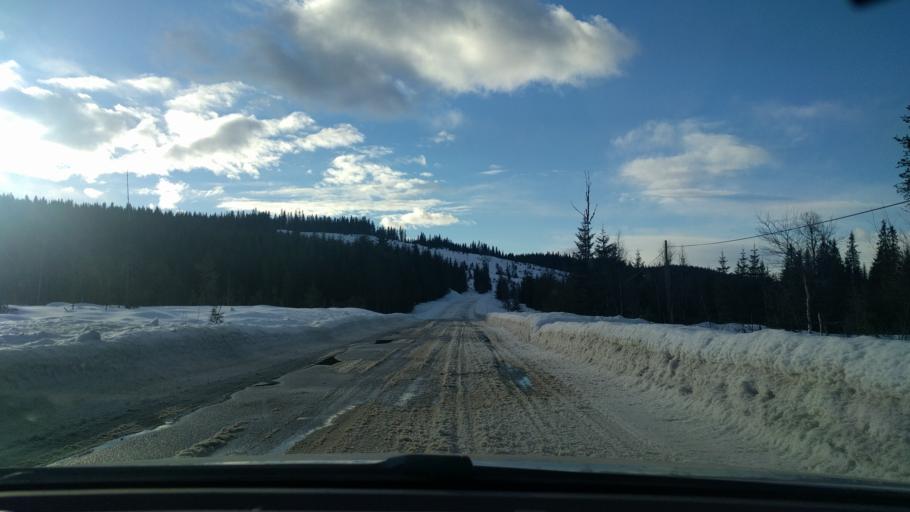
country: NO
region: Hedmark
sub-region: Trysil
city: Innbygda
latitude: 61.1085
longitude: 12.0980
